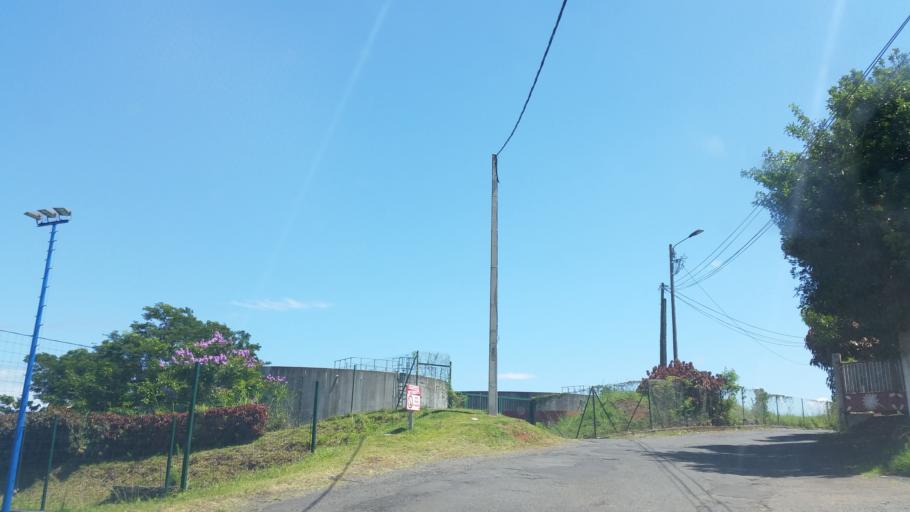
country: RE
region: Reunion
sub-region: Reunion
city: Sainte-Marie
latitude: -20.9308
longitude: 55.5304
